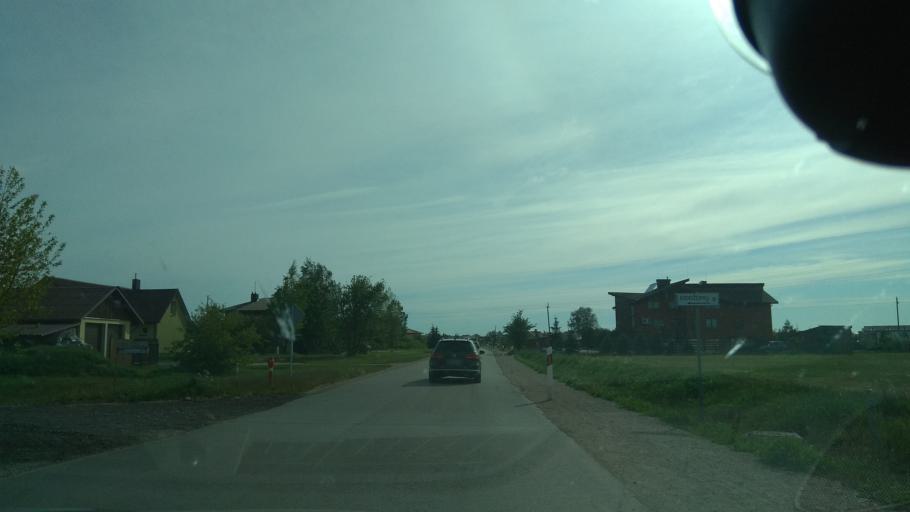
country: LT
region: Klaipedos apskritis
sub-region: Klaipeda
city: Klaipeda
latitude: 55.7558
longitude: 21.1849
